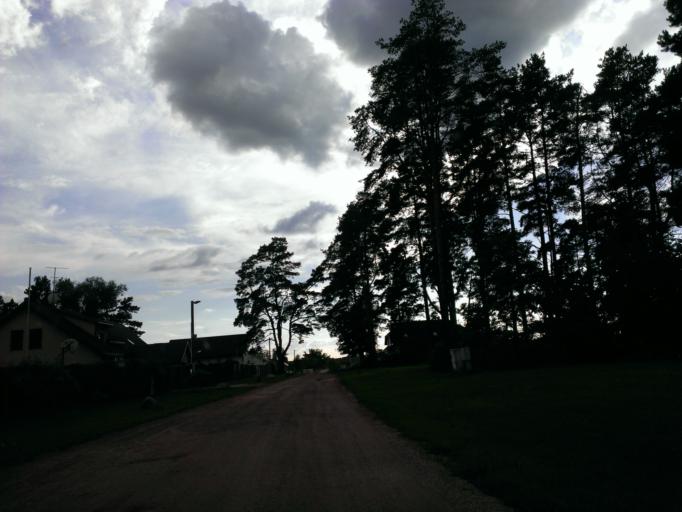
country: LV
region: Ikskile
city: Ikskile
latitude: 56.8370
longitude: 24.4847
